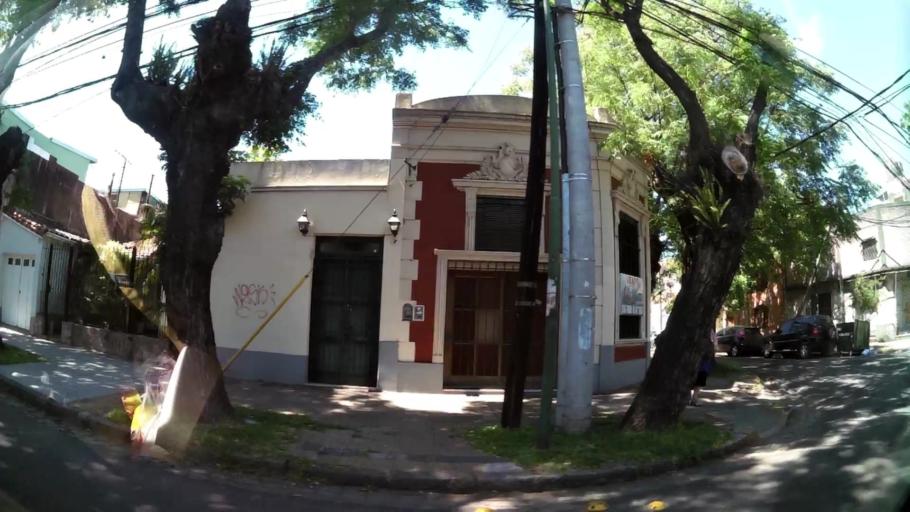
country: AR
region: Buenos Aires
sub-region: Partido de San Isidro
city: San Isidro
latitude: -34.4692
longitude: -58.5189
